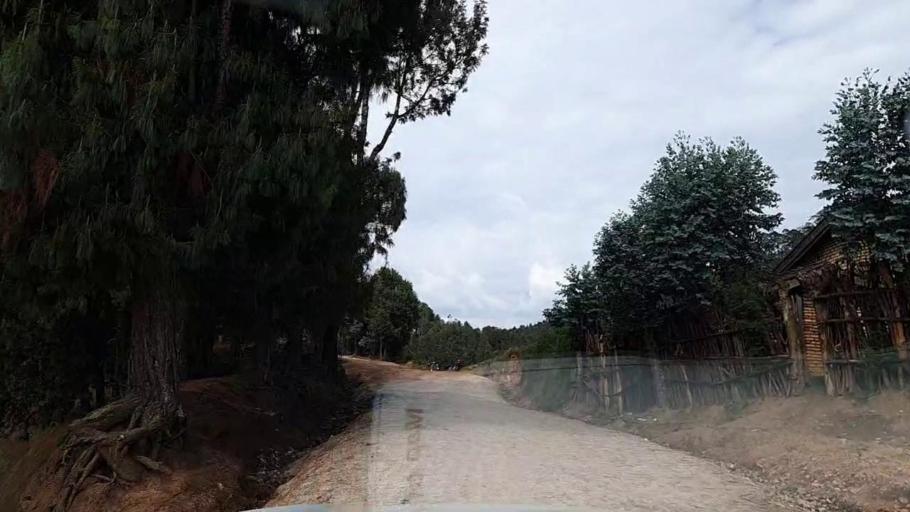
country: RW
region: Southern Province
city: Nzega
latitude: -2.4139
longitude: 29.4531
